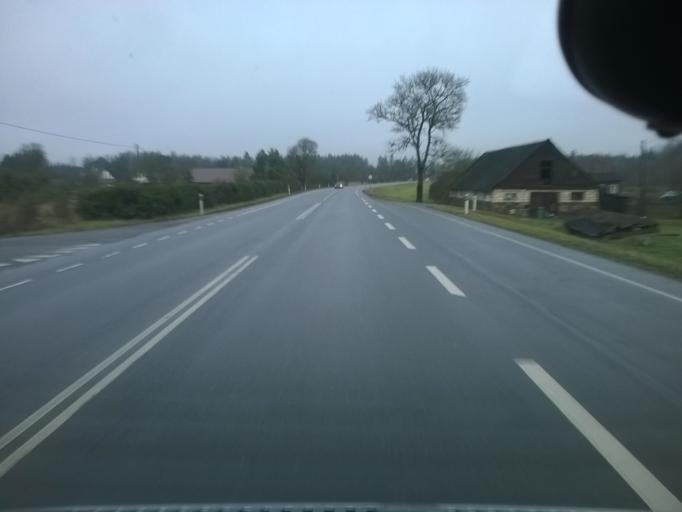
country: EE
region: Harju
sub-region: Saku vald
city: Saku
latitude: 59.3082
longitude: 24.7446
